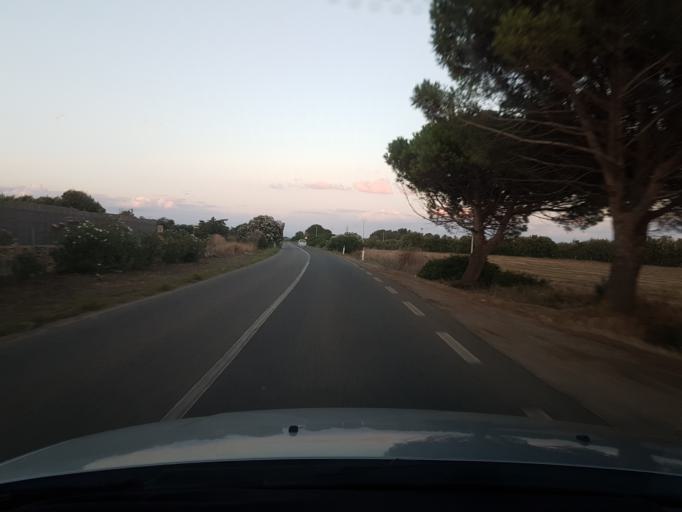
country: IT
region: Sardinia
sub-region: Provincia di Oristano
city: Riola Sardo
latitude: 40.0213
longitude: 8.4544
